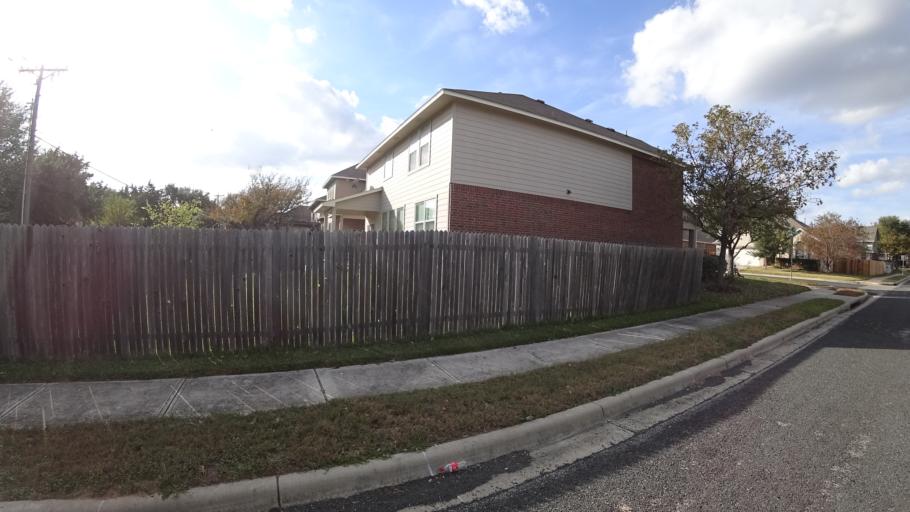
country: US
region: Texas
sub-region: Williamson County
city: Brushy Creek
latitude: 30.5095
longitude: -97.7214
